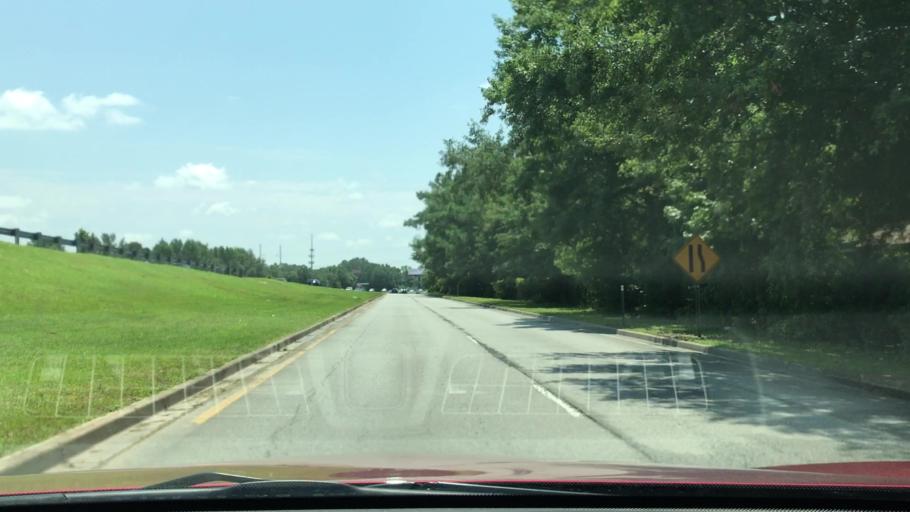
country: US
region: South Carolina
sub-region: Charleston County
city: North Charleston
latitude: 32.8518
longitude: -80.0203
